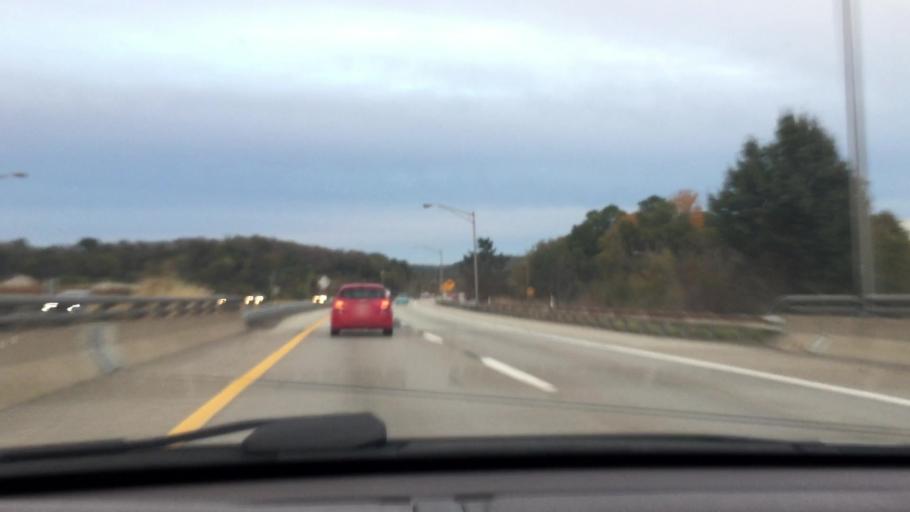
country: US
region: Pennsylvania
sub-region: Allegheny County
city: Oakmont
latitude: 40.5406
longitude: -79.8405
